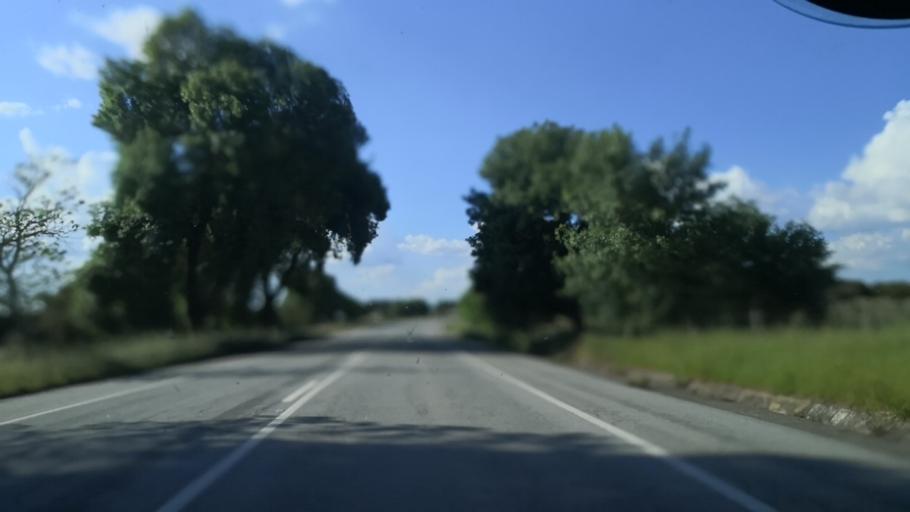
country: PT
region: Portalegre
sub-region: Portalegre
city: Urra
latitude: 39.0834
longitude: -7.4377
